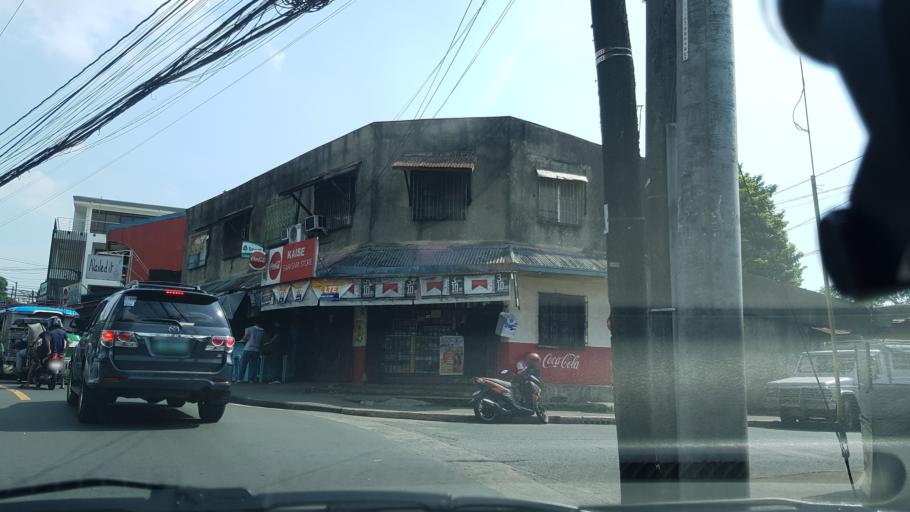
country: PH
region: Calabarzon
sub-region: Province of Rizal
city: Antipolo
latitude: 14.6615
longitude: 121.1125
